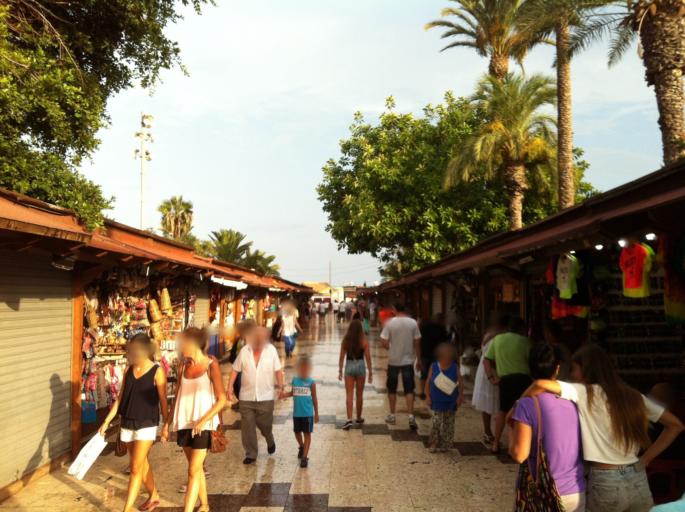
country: ES
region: Valencia
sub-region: Provincia de Alicante
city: Torrevieja
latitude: 37.9746
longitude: -0.6789
